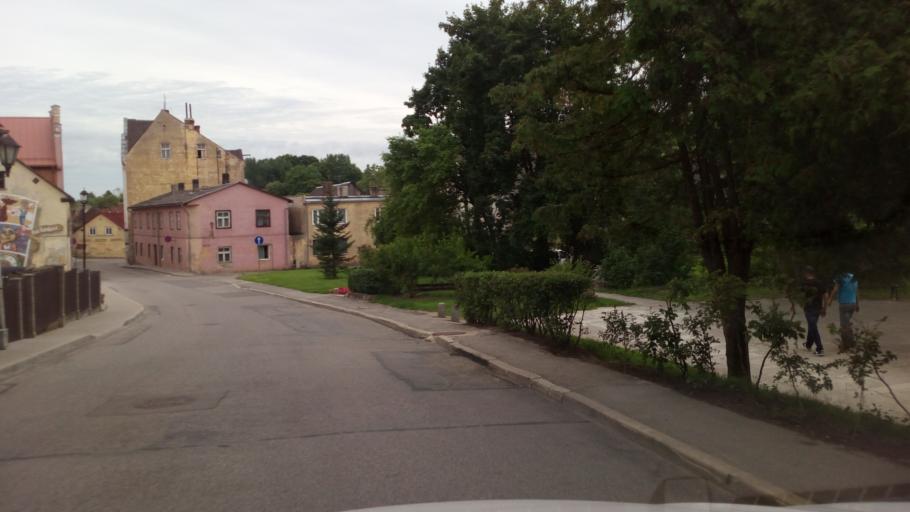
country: LV
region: Kandava
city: Kandava
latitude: 57.0381
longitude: 22.7765
